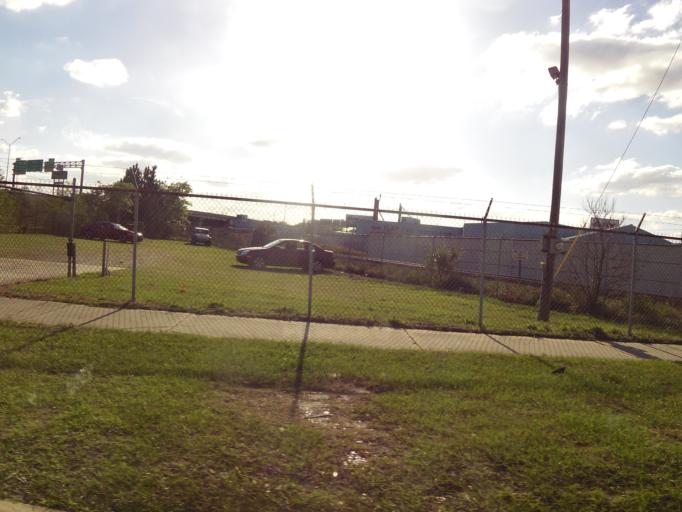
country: US
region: Florida
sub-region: Duval County
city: Jacksonville
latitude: 30.3219
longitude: -81.6915
